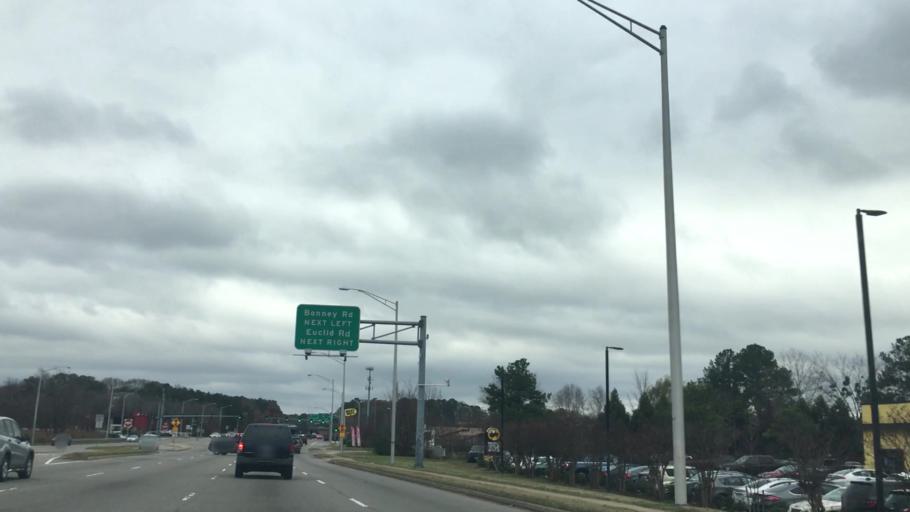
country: US
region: Virginia
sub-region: City of Chesapeake
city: Chesapeake
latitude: 36.8400
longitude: -76.1370
